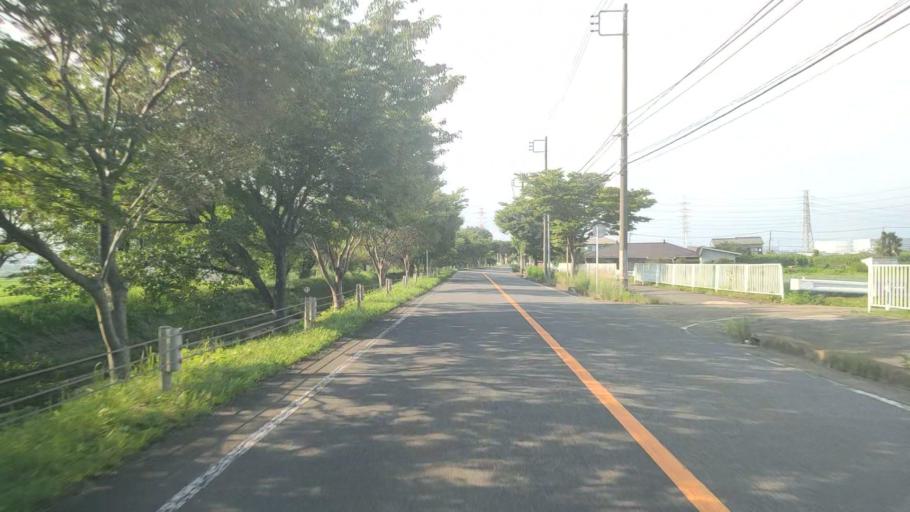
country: JP
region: Kanagawa
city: Isehara
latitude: 35.3935
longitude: 139.3379
